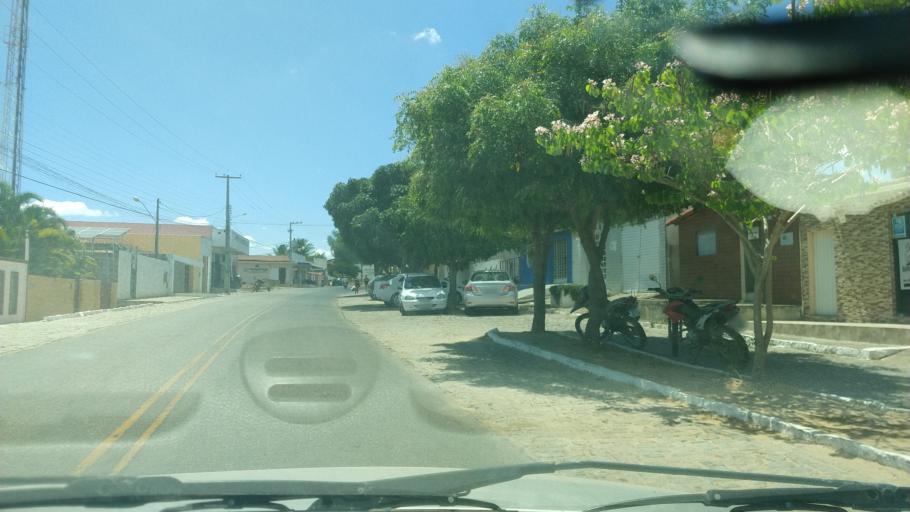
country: BR
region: Rio Grande do Norte
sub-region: Cerro Cora
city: Cerro Cora
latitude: -6.0518
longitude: -36.3540
